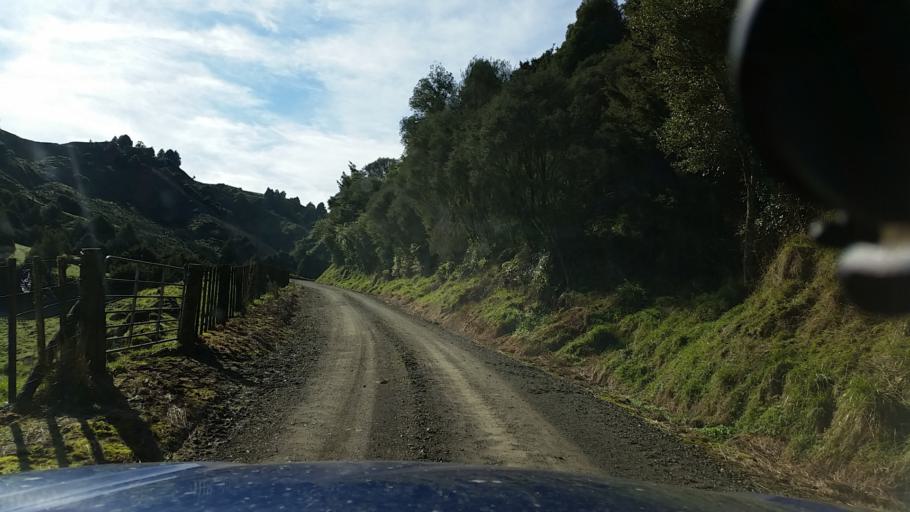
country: NZ
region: Taranaki
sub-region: New Plymouth District
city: Waitara
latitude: -39.0523
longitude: 174.7547
